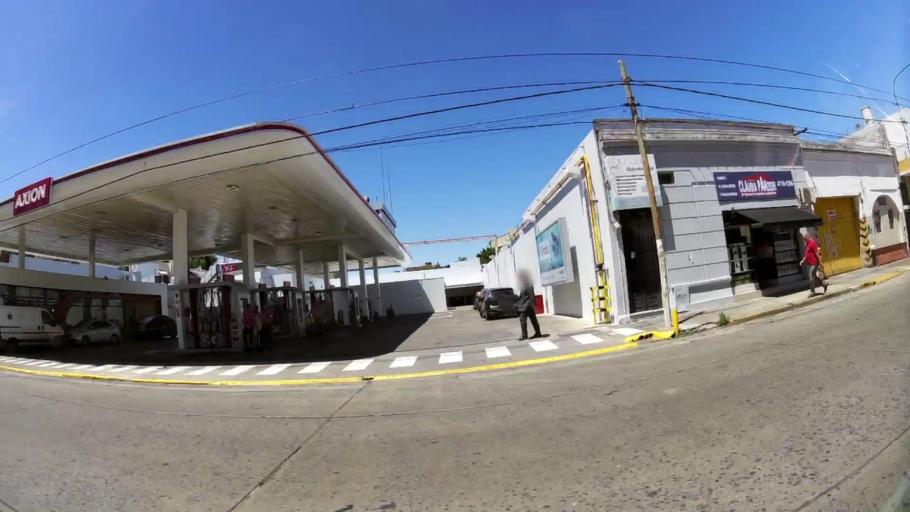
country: AR
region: Buenos Aires
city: Caseros
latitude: -34.5997
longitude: -58.5617
